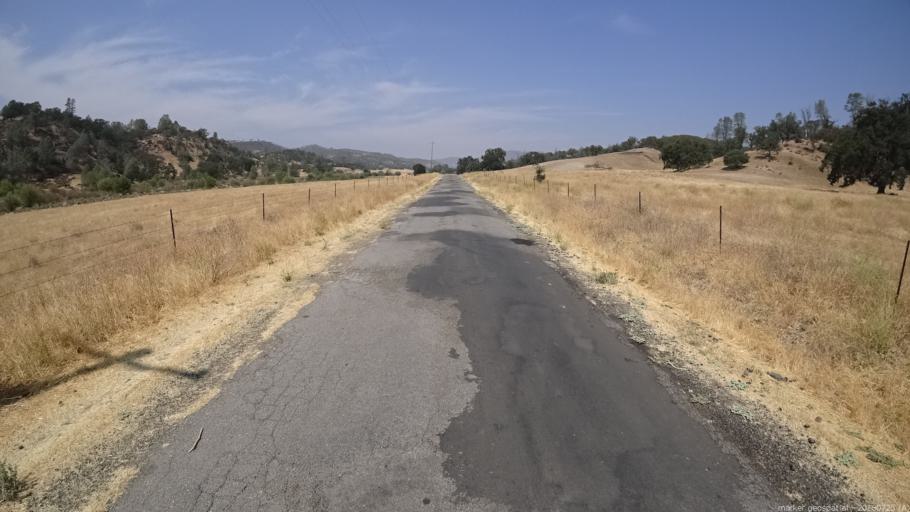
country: US
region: California
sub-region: Fresno County
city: Coalinga
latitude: 35.9429
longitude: -120.4648
